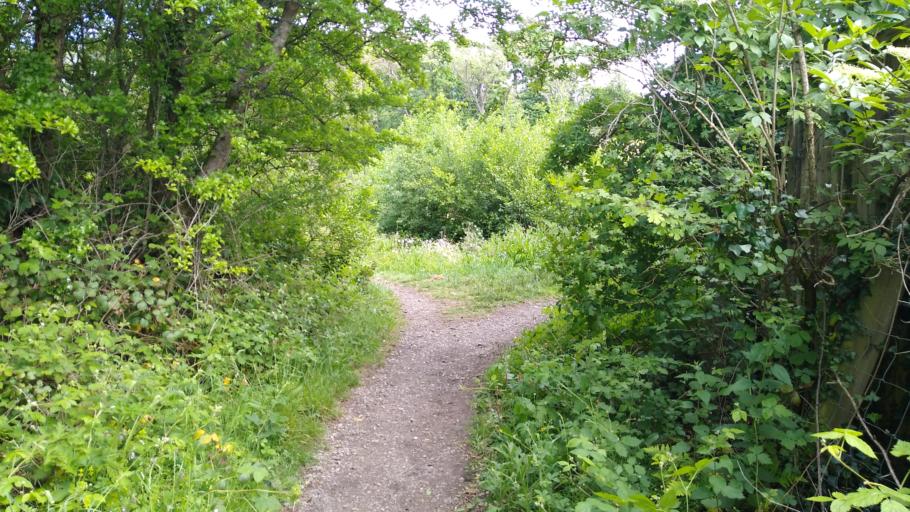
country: GB
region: England
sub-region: Cumbria
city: Flimby
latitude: 54.6607
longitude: -3.4944
